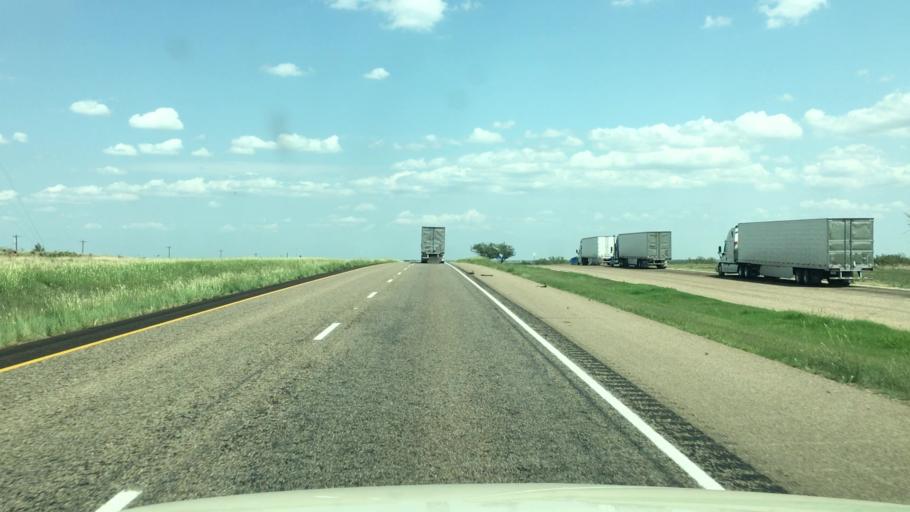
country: US
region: Texas
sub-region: Armstrong County
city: Claude
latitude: 35.0327
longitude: -101.1521
